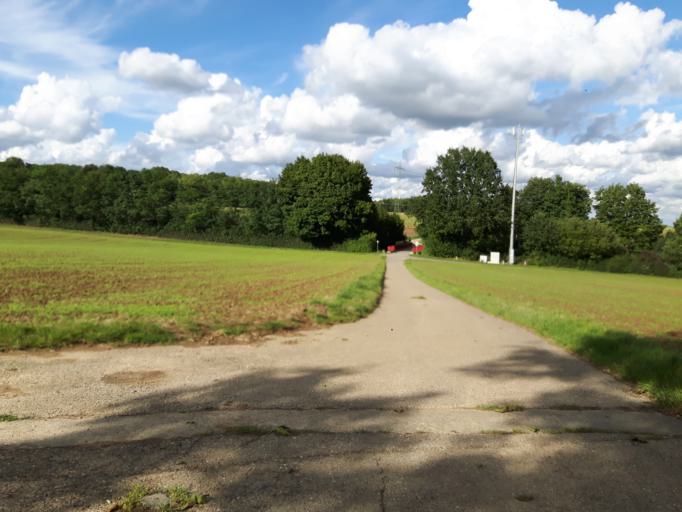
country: DE
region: Baden-Wuerttemberg
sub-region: Regierungsbezirk Stuttgart
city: Bad Rappenau
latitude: 49.2389
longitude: 9.1224
